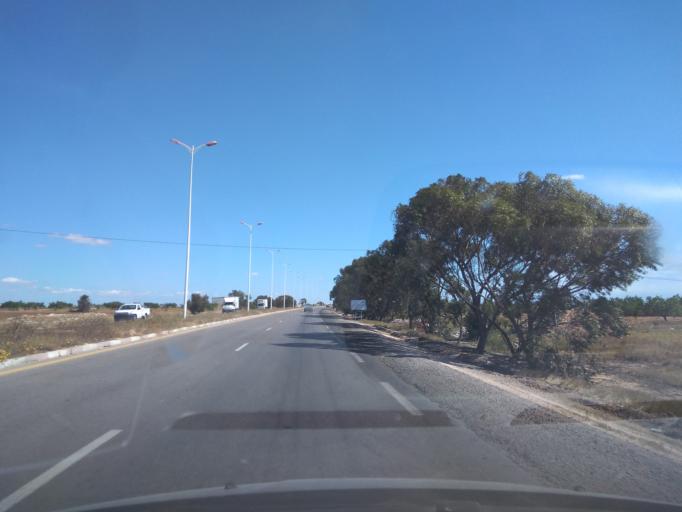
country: TN
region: Safaqis
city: Al Qarmadah
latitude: 34.8414
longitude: 10.7390
